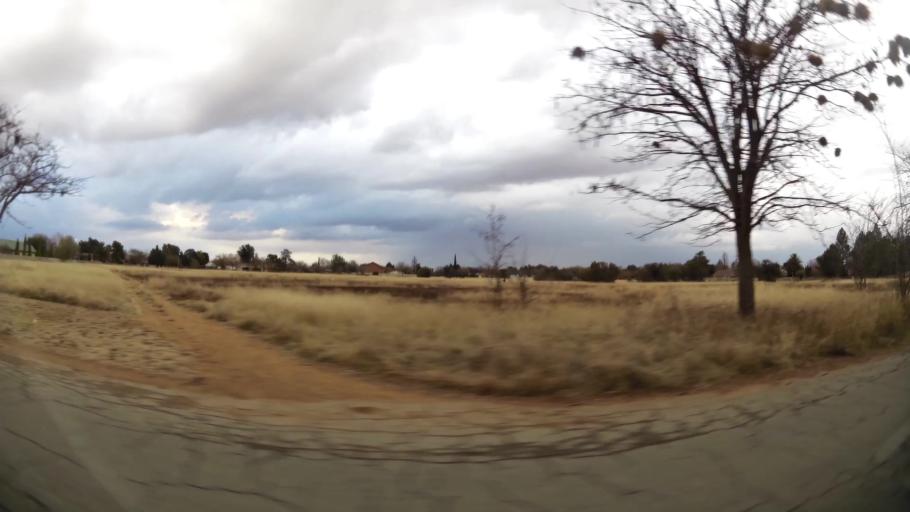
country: ZA
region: Orange Free State
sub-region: Lejweleputswa District Municipality
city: Welkom
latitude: -27.9678
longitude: 26.7229
